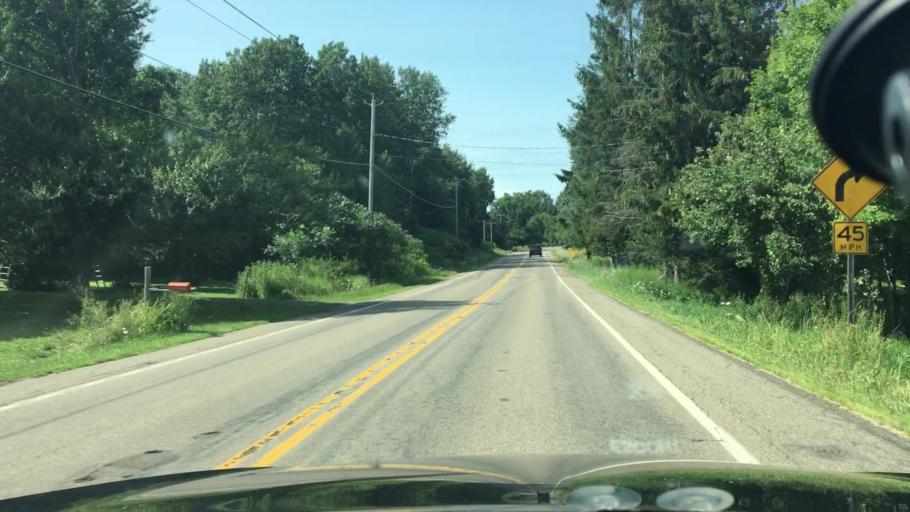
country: US
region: New York
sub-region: Chautauqua County
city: Brocton
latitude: 42.2689
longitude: -79.3519
